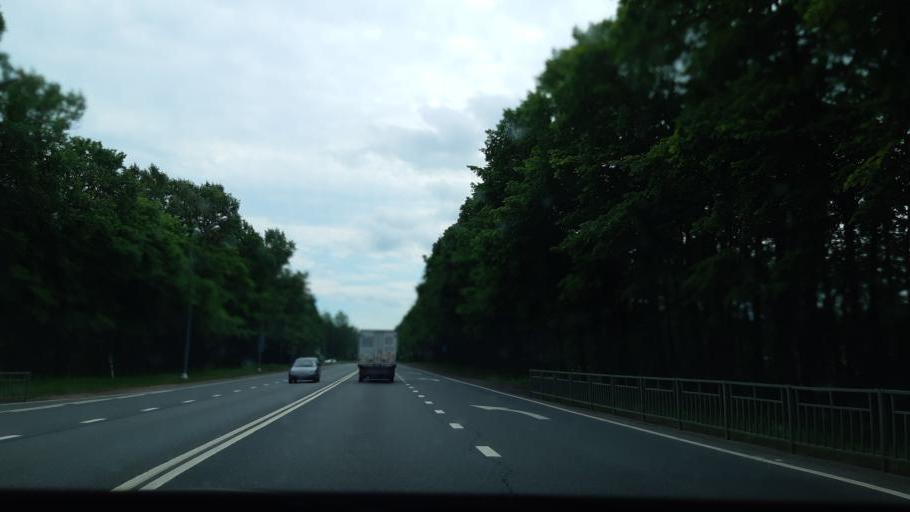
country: RU
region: Moskovskaya
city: Dorokhovo
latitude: 55.4732
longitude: 36.3565
